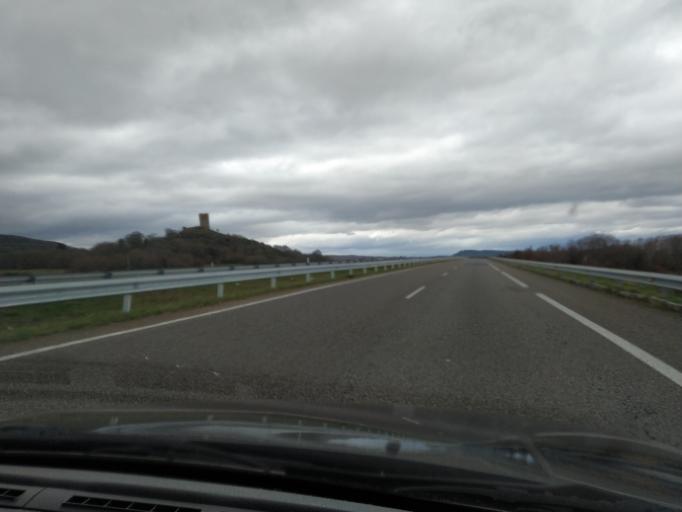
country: ES
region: Galicia
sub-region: Provincia de Ourense
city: Xinzo de Limia
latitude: 42.1173
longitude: -7.7380
